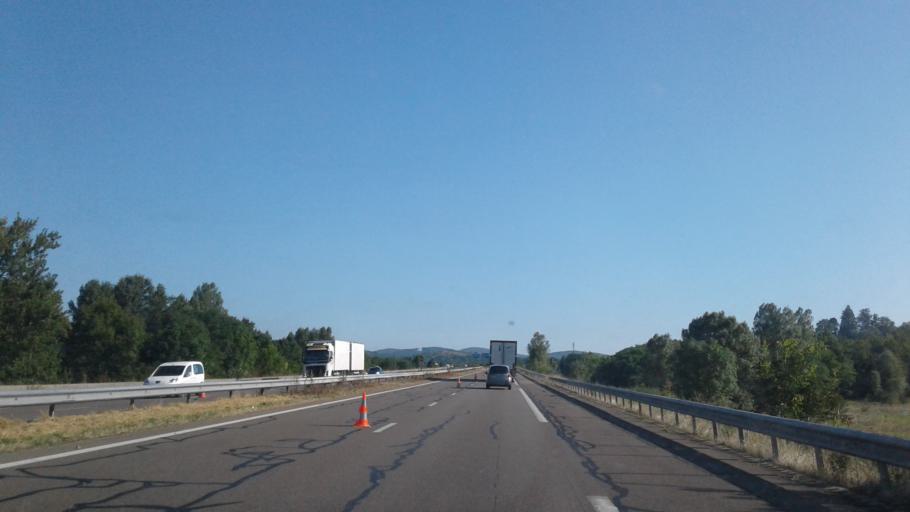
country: FR
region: Rhone-Alpes
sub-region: Departement de l'Ain
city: Saint-Martin-du-Mont
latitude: 46.0540
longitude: 5.3277
